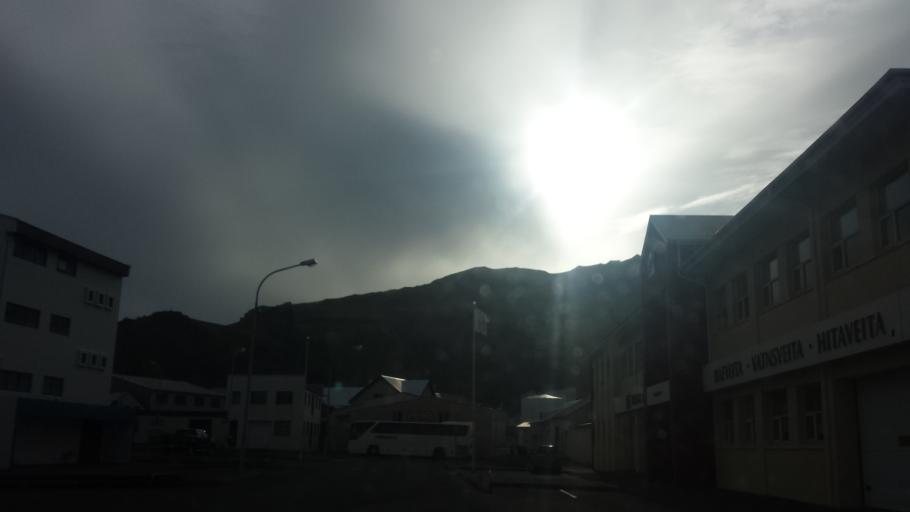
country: IS
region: South
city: Vestmannaeyjar
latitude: 63.4429
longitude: -20.2722
